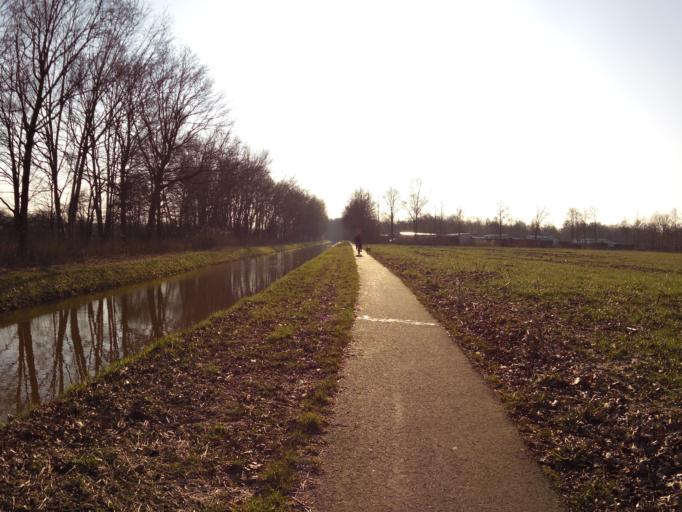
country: NL
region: North Brabant
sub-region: Gemeente Maasdonk
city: Geffen
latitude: 51.7049
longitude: 5.4381
